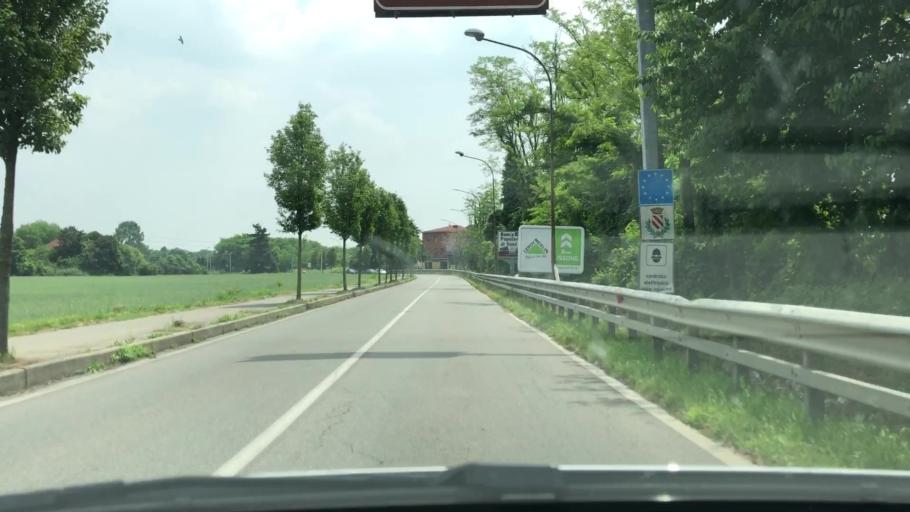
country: IT
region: Lombardy
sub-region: Provincia di Monza e Brianza
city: Desio
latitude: 45.6271
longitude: 9.1815
